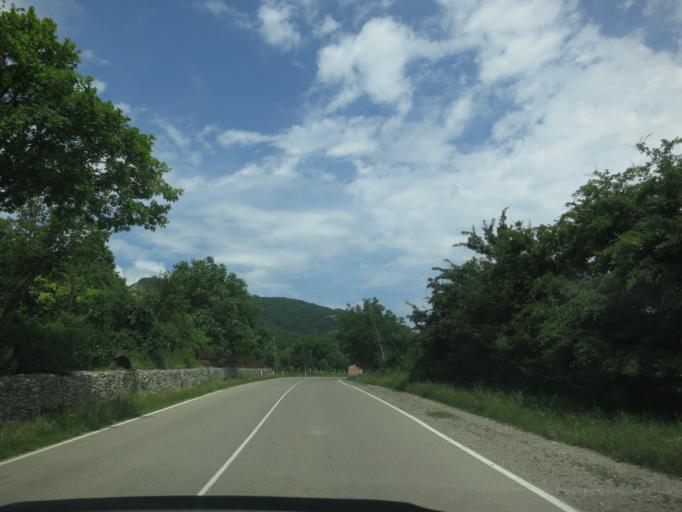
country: GE
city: Didi Lilo
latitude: 41.8316
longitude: 45.1359
